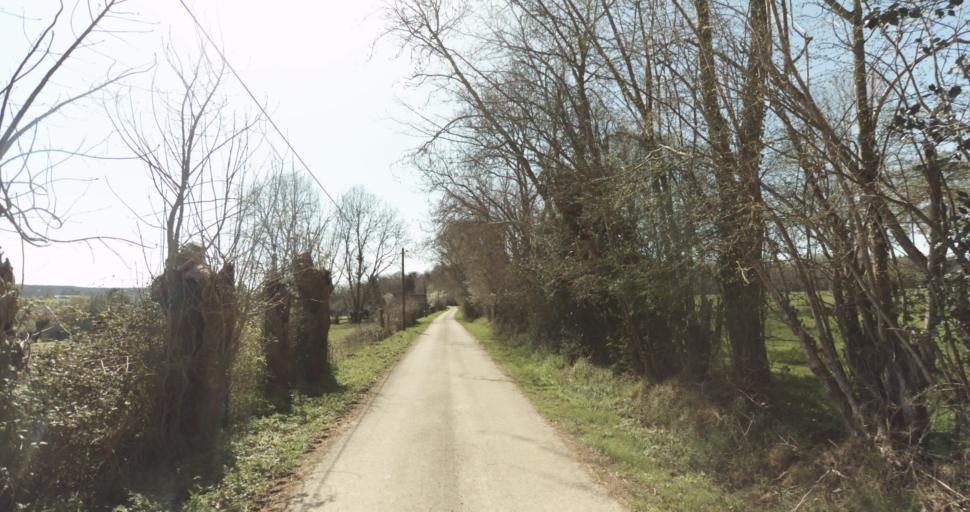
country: FR
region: Lower Normandy
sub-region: Departement du Calvados
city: Saint-Pierre-sur-Dives
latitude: 48.9929
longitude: 0.0565
